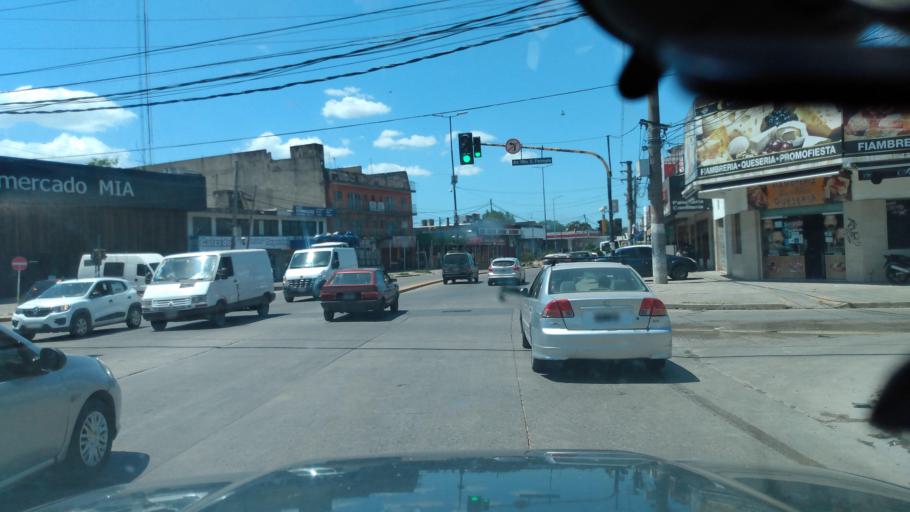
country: AR
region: Buenos Aires
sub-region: Partido de Merlo
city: Merlo
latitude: -34.5689
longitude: -58.7427
